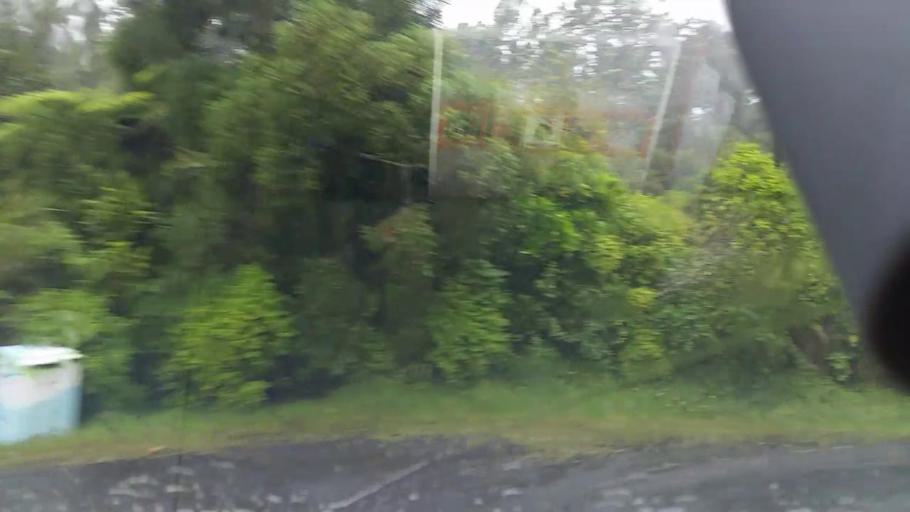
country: NZ
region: Auckland
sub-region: Auckland
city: Waitakere
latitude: -36.9079
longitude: 174.5686
